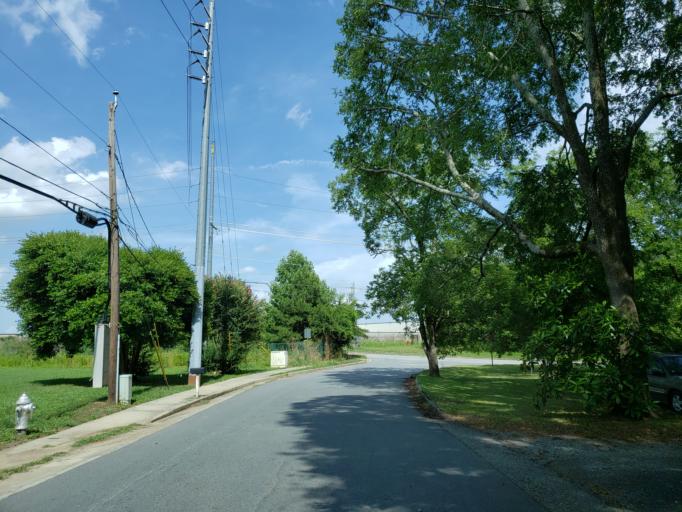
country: US
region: Georgia
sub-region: Cobb County
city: Fair Oaks
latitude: 33.9163
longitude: -84.5404
